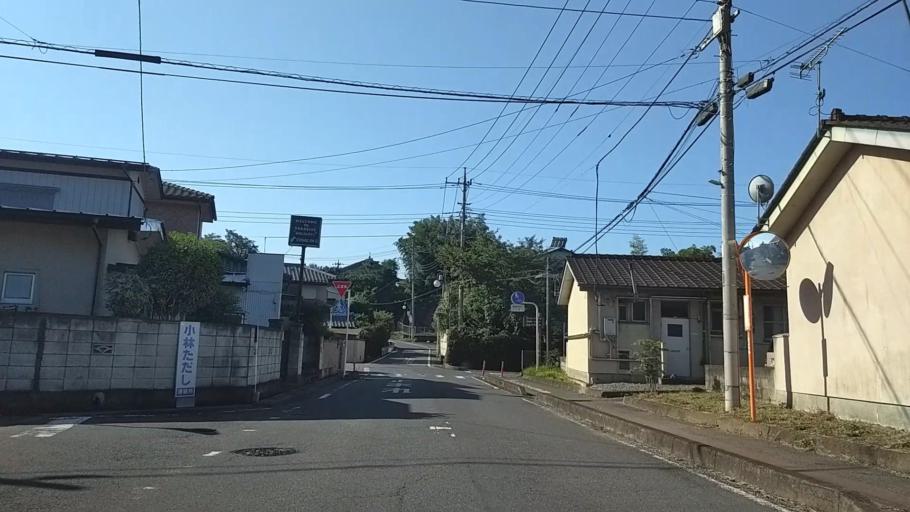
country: JP
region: Gunma
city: Annaka
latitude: 36.3351
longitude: 138.9091
